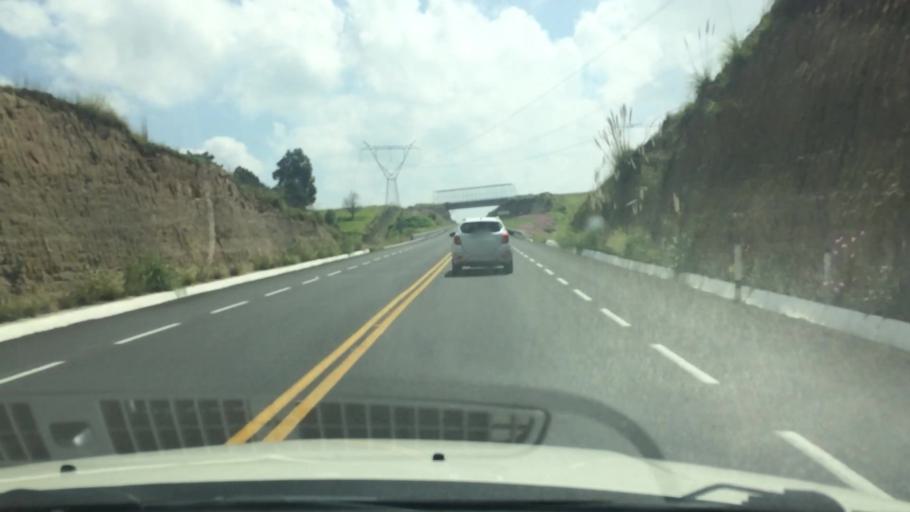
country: MX
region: Mexico
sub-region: Almoloya de Juarez
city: San Pedro de la Hortaliza (Ejido Almoloyan)
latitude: 19.3782
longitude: -99.8509
